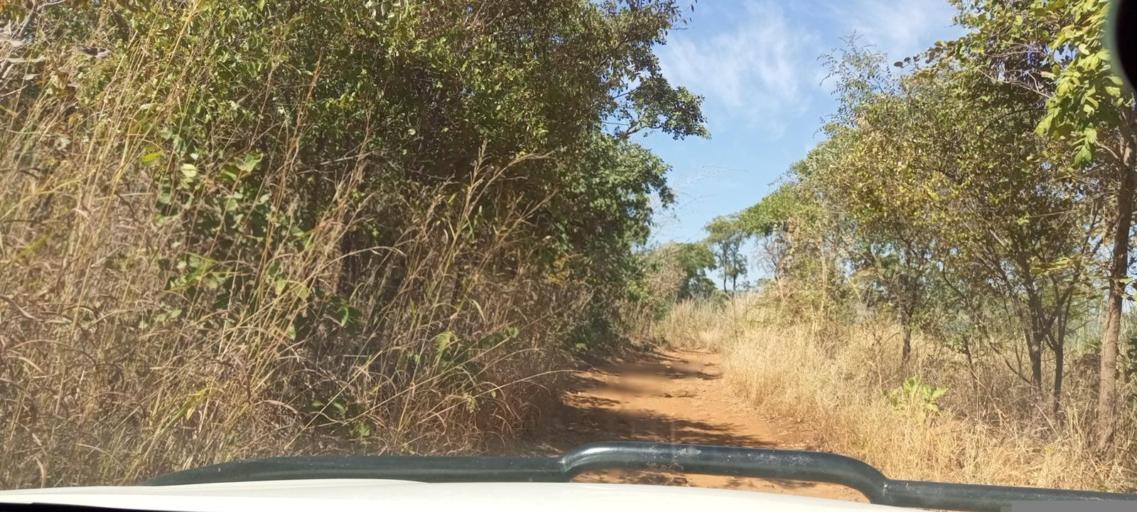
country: ML
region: Koulikoro
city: Kangaba
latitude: 12.3259
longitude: -8.6700
